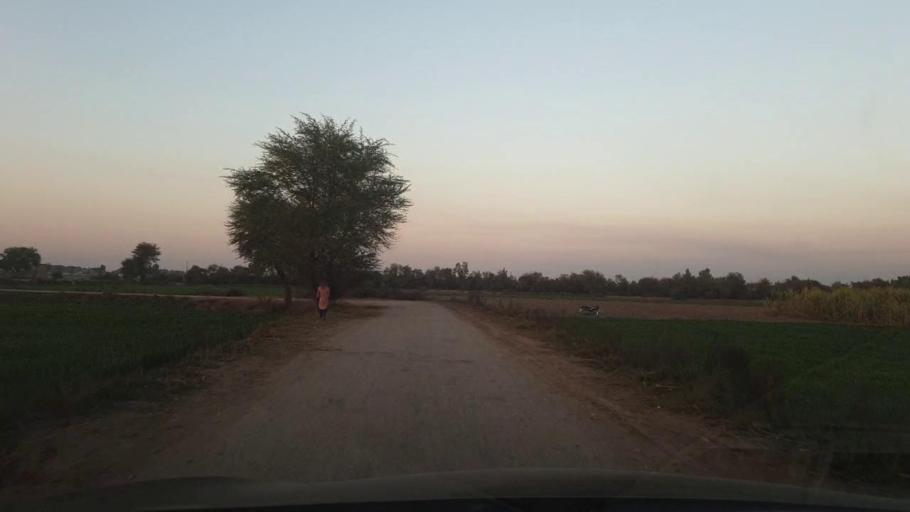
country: PK
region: Sindh
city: Ubauro
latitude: 28.1730
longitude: 69.6359
